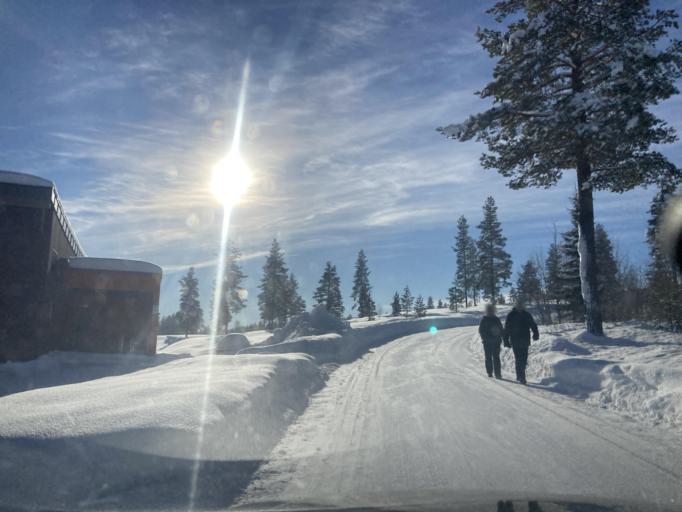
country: NO
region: Hedmark
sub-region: Trysil
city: Innbygda
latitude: 61.3000
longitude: 12.2442
